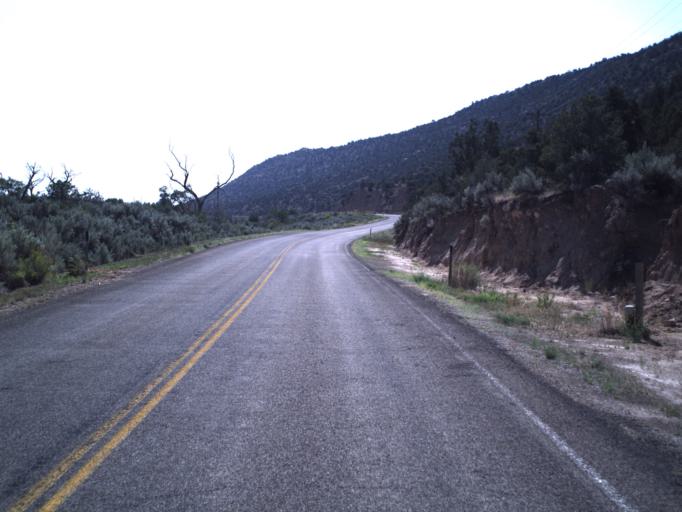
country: US
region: Utah
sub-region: Duchesne County
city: Duchesne
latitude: 40.2856
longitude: -110.4945
